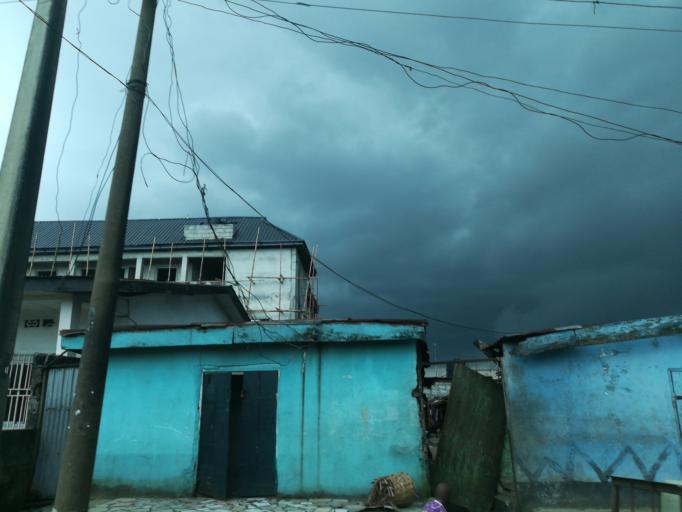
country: NG
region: Rivers
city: Port Harcourt
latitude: 4.8011
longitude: 6.9883
